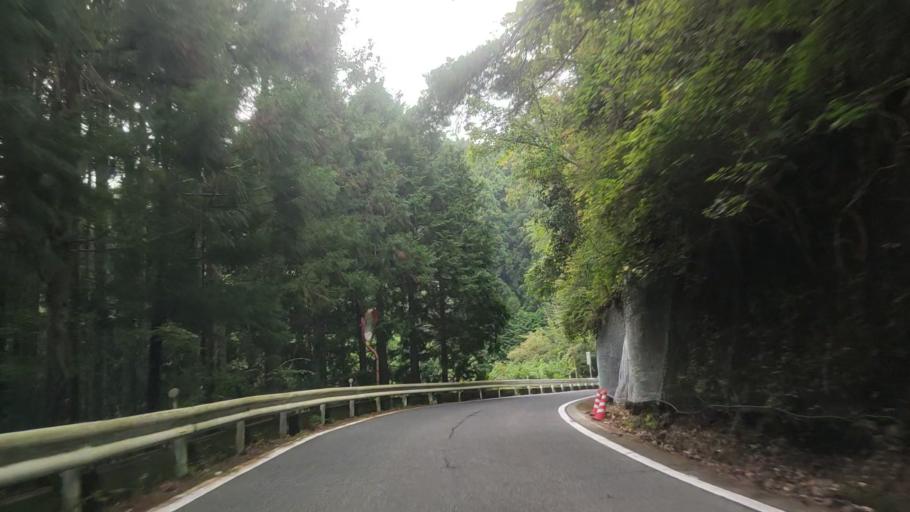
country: JP
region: Wakayama
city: Koya
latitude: 34.2371
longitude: 135.5478
